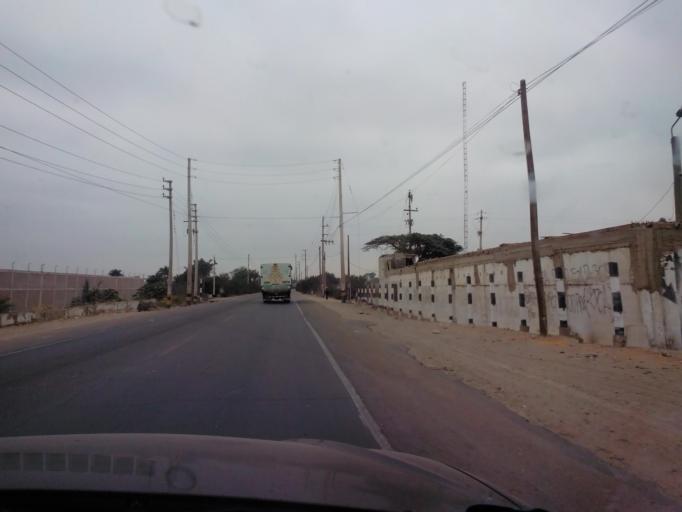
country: PE
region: Ica
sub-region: Provincia de Chincha
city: Chincha Baja
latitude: -13.4617
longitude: -76.1364
